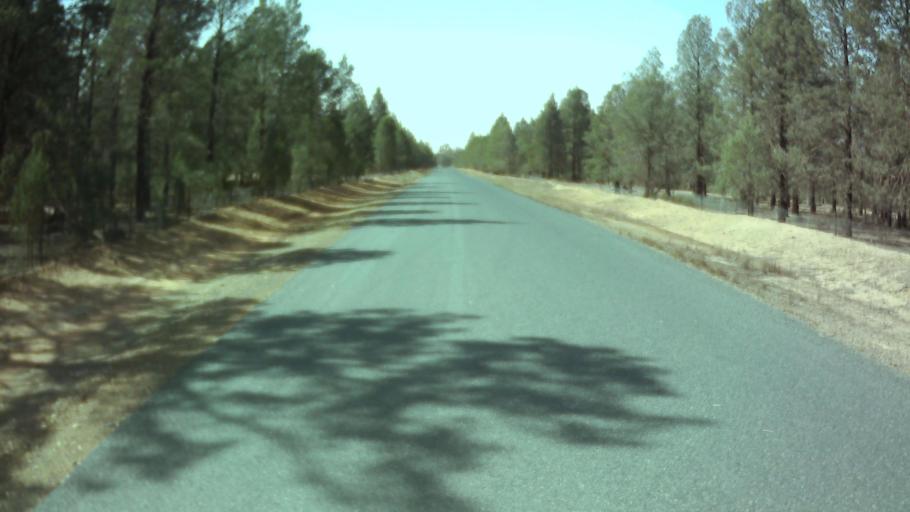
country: AU
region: New South Wales
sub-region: Weddin
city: Grenfell
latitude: -33.9063
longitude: 147.9197
